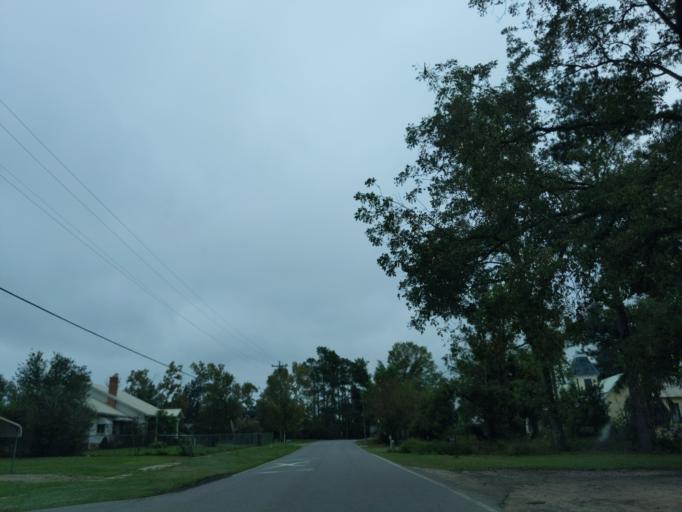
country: US
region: Florida
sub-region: Jackson County
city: Sneads
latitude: 30.7073
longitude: -84.9243
